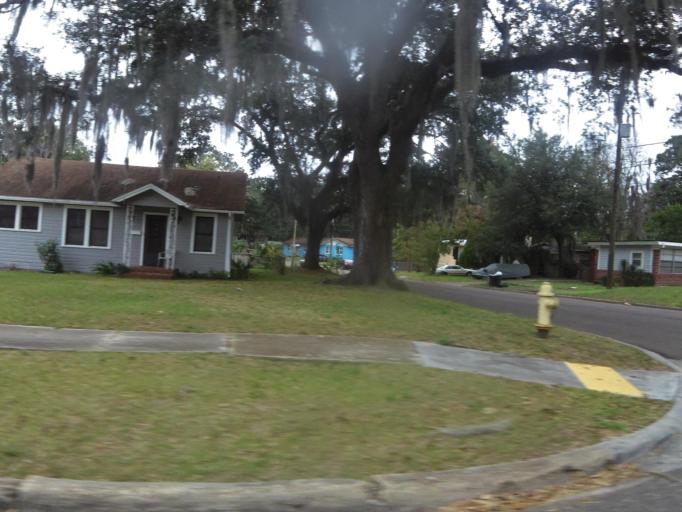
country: US
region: Florida
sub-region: Duval County
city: Jacksonville
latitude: 30.3830
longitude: -81.6577
